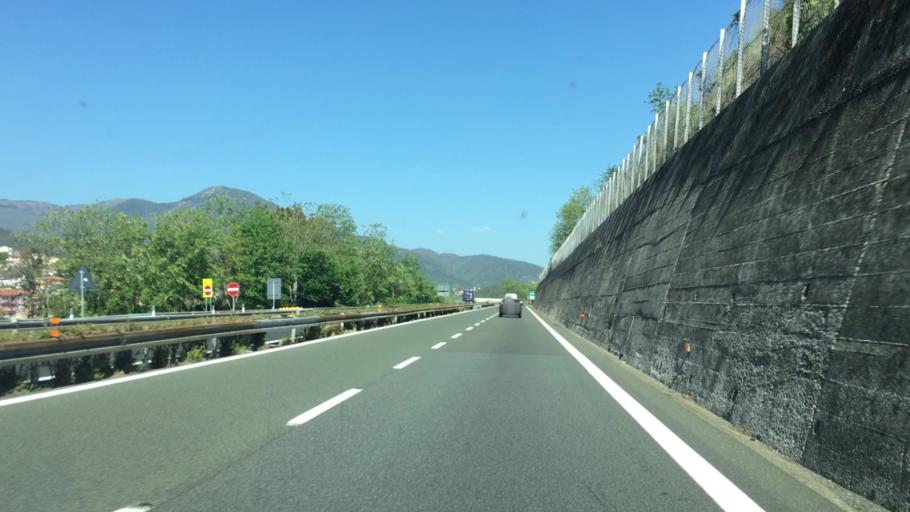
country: IT
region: Liguria
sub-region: Provincia di Genova
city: Casarza Ligure
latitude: 44.2682
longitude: 9.4370
